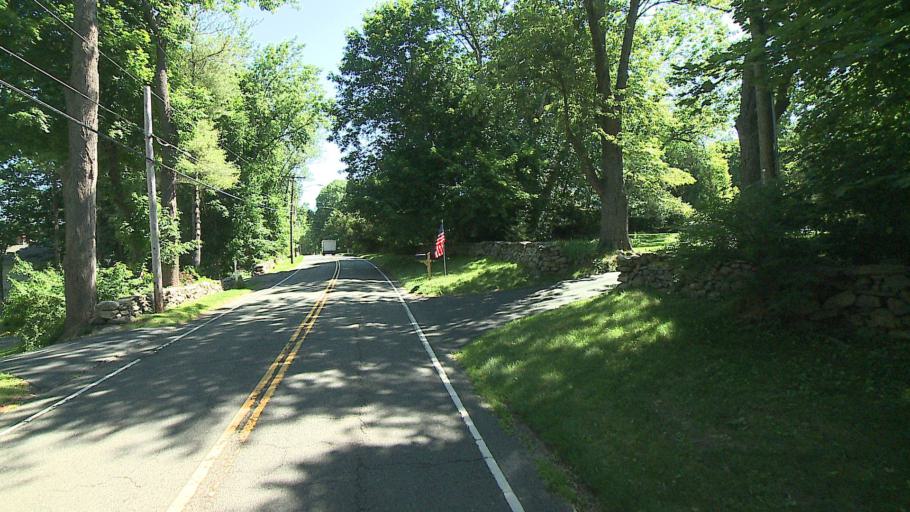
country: US
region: Connecticut
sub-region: Fairfield County
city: Ridgefield
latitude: 41.2639
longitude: -73.5107
